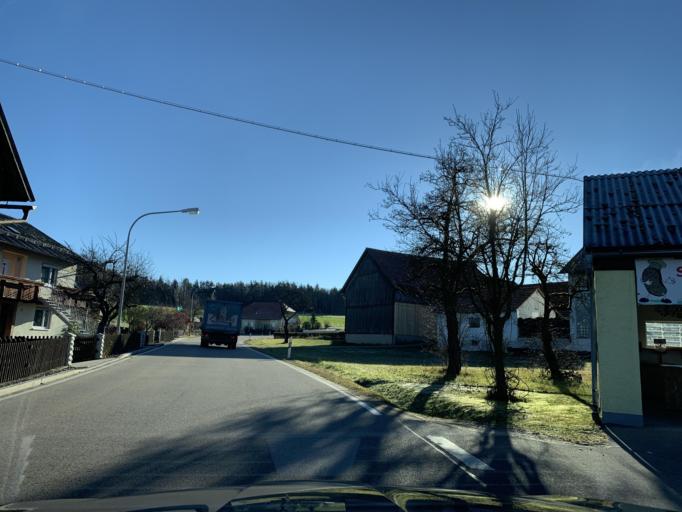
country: DE
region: Bavaria
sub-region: Upper Palatinate
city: Oberviechtach
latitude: 49.4404
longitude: 12.4155
